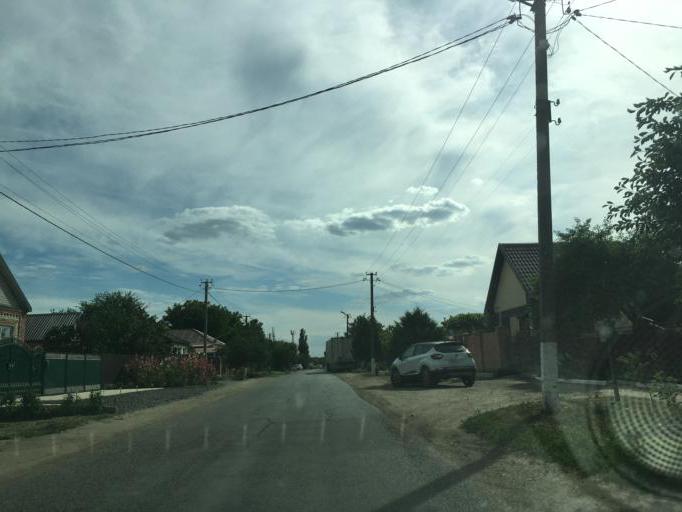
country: RU
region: Krasnodarskiy
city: Kushchevskaya
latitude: 46.5584
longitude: 39.6319
